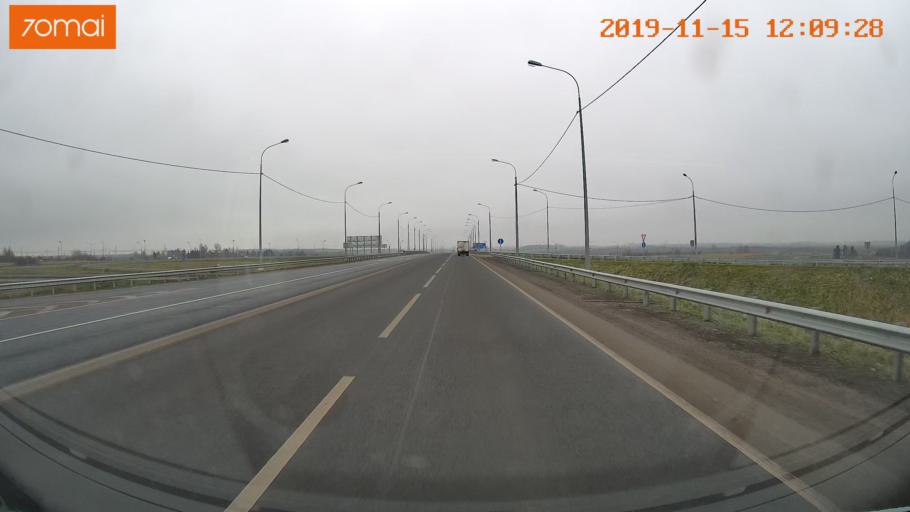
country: RU
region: Vologda
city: Vologda
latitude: 59.2155
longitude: 39.7705
